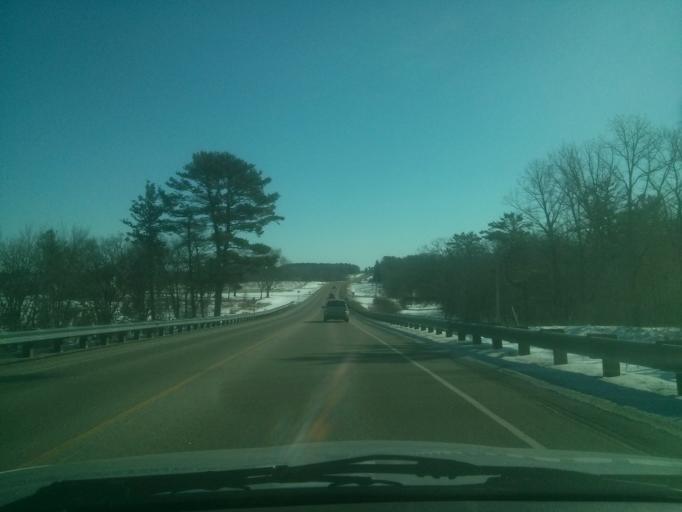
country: US
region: Wisconsin
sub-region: Saint Croix County
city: New Richmond
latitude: 45.1372
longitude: -92.4209
